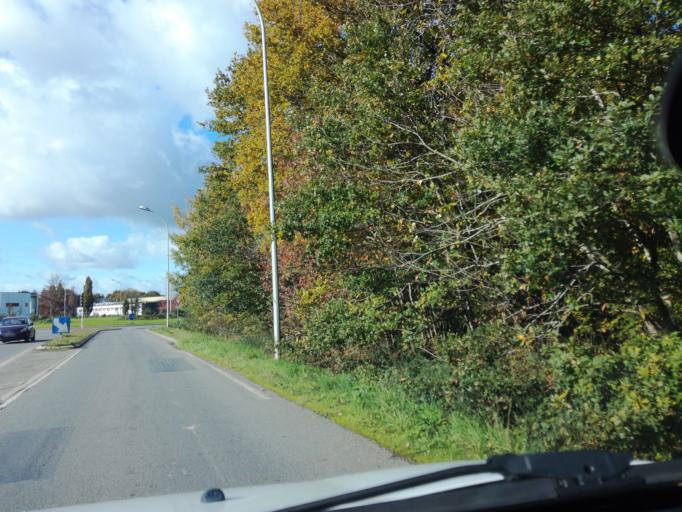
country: FR
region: Brittany
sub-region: Departement d'Ille-et-Vilaine
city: Mordelles
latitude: 48.0699
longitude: -1.8296
